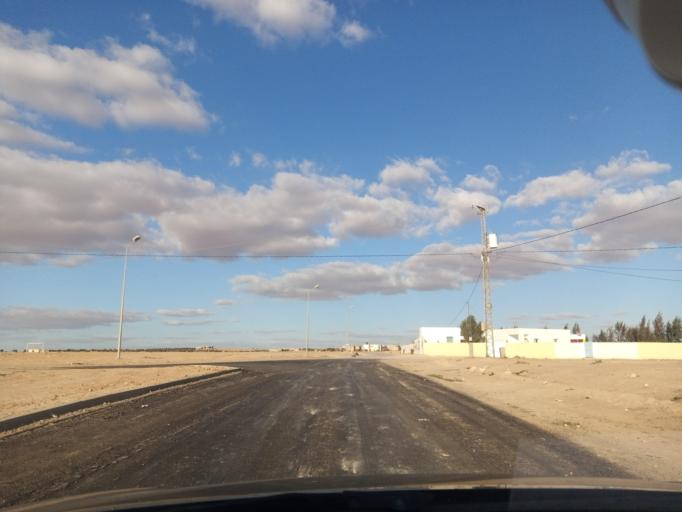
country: TN
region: Safaqis
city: Bi'r `Ali Bin Khalifah
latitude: 34.7130
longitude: 10.4225
